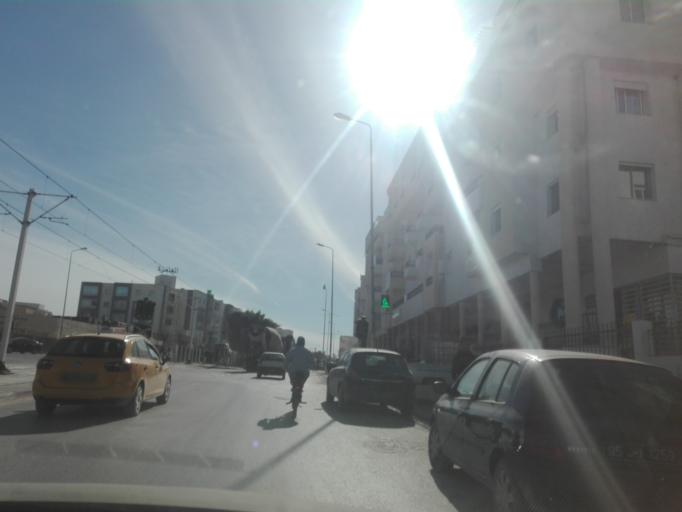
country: TN
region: Bin 'Arus
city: Ben Arous
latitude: 36.7209
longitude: 10.2159
